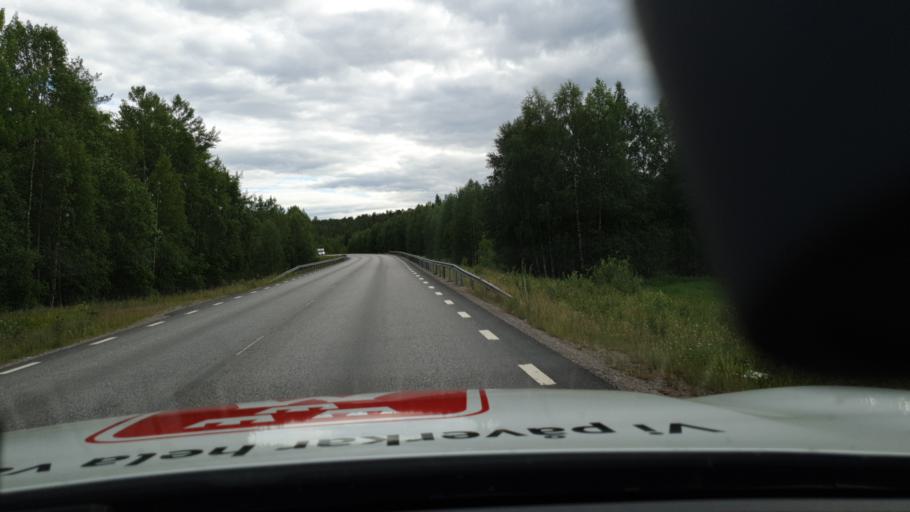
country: SE
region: Norrbotten
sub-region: Overkalix Kommun
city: OEverkalix
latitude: 66.3560
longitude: 22.8297
